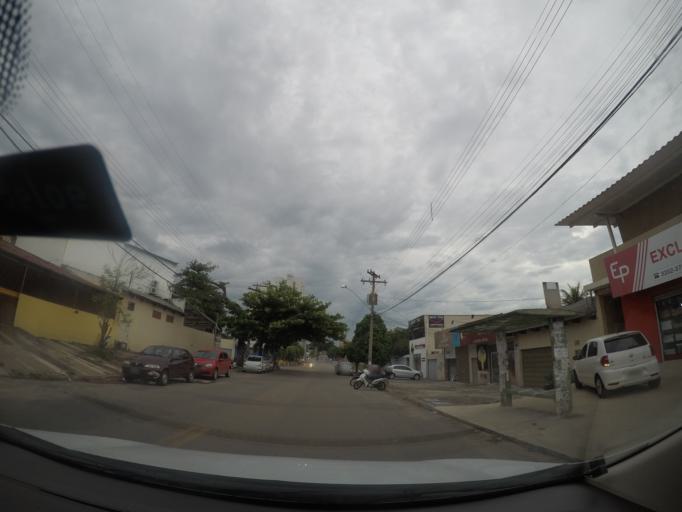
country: BR
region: Goias
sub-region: Goiania
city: Goiania
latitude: -16.6567
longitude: -49.2432
